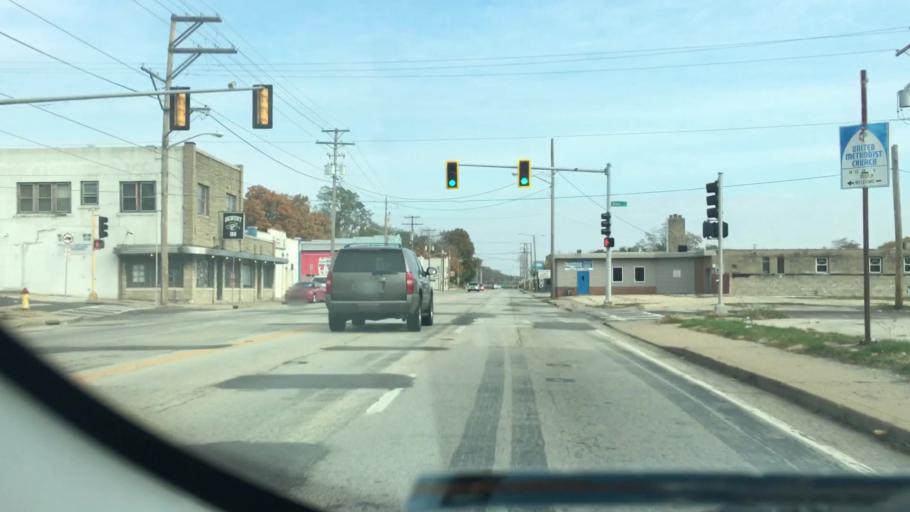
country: US
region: Illinois
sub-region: Peoria County
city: North Peoria
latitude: 40.7172
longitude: -89.5591
